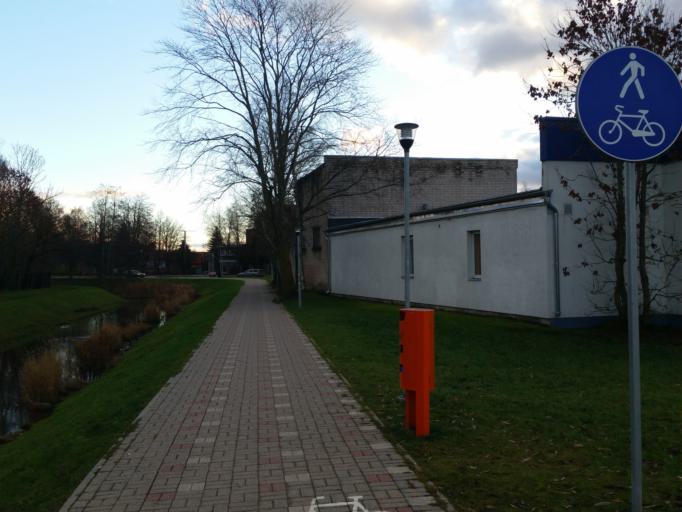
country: LV
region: Ventspils
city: Ventspils
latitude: 57.3849
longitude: 21.5761
